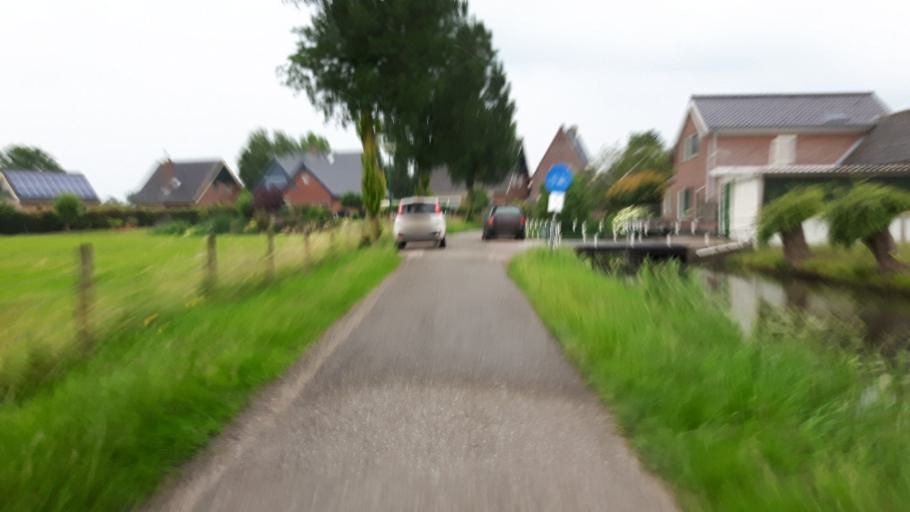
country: NL
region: Utrecht
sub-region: Gemeente IJsselstein
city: IJsselstein
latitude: 51.9855
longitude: 5.0293
